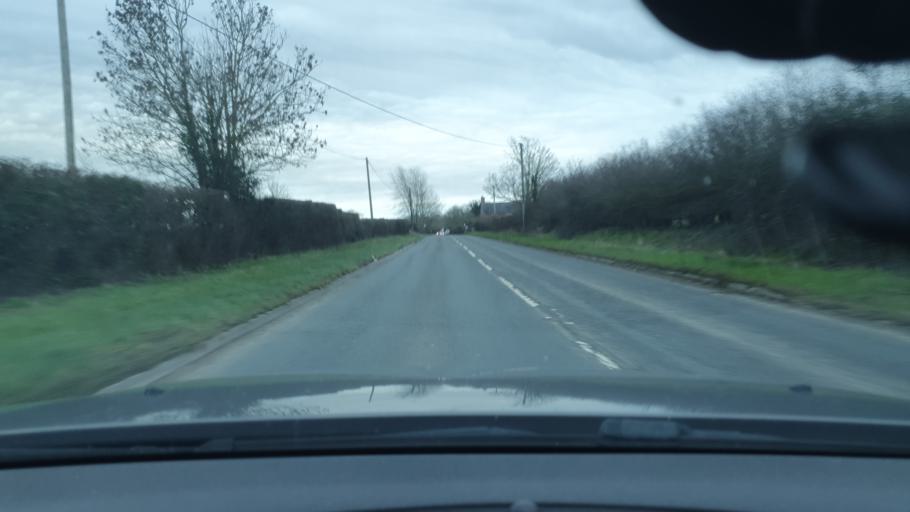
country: GB
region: England
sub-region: Wiltshire
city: Melksham
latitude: 51.3397
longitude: -2.1324
